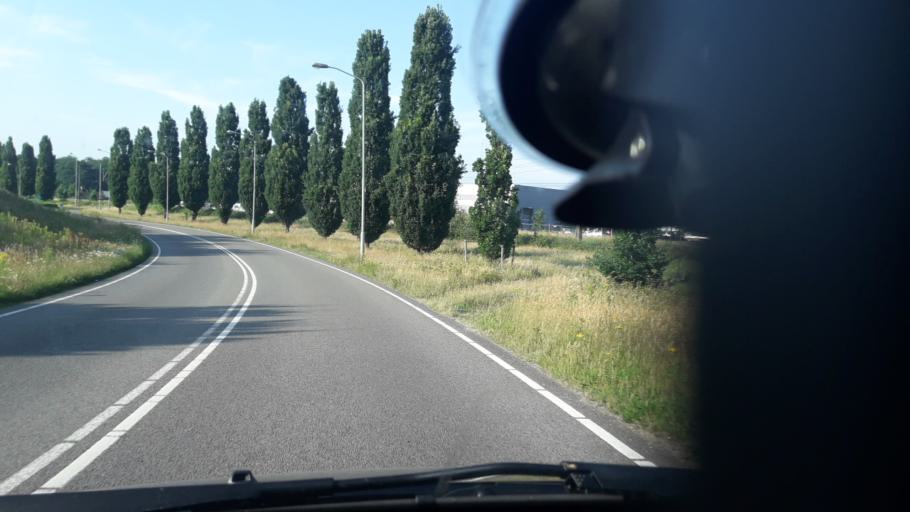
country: NL
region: Gelderland
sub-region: Gemeente Harderwijk
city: Harderwijk
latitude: 52.3251
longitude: 5.6115
